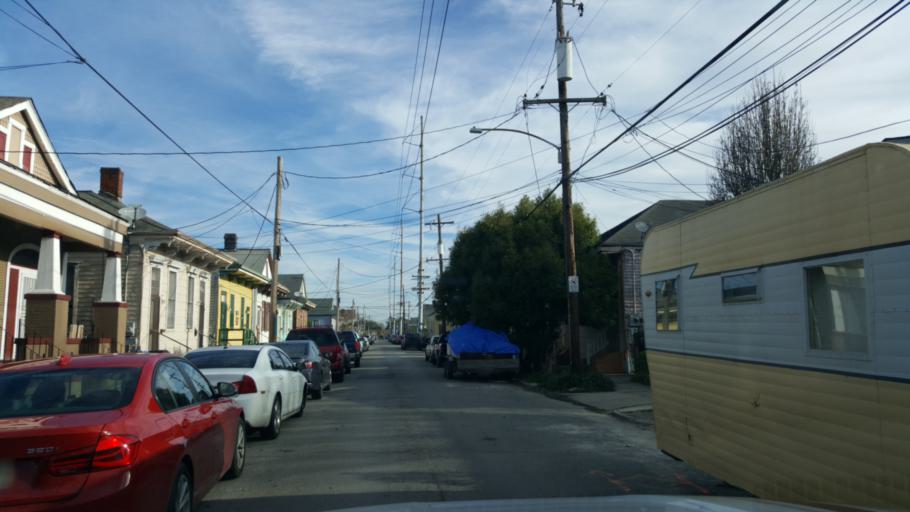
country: US
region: Louisiana
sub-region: Orleans Parish
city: New Orleans
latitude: 29.9726
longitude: -90.0701
